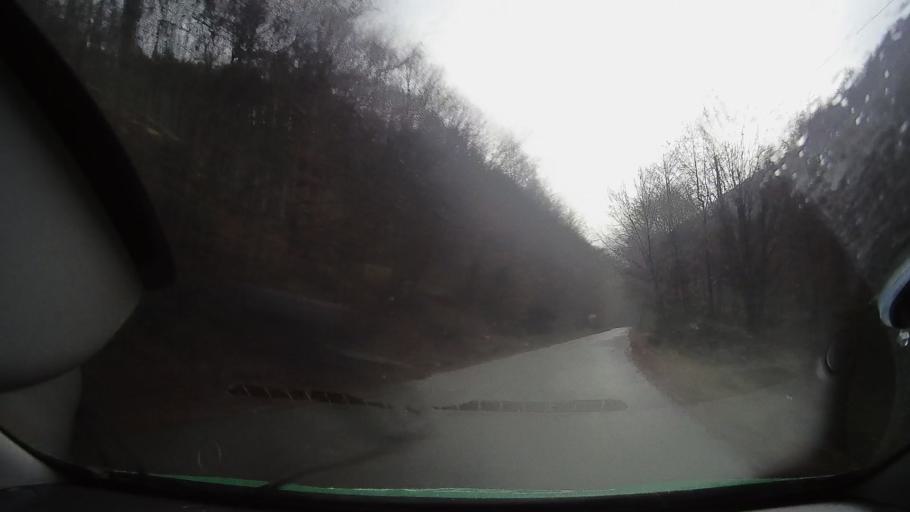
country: RO
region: Hunedoara
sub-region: Comuna Ribita
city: Ribita
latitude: 46.2842
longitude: 22.7365
